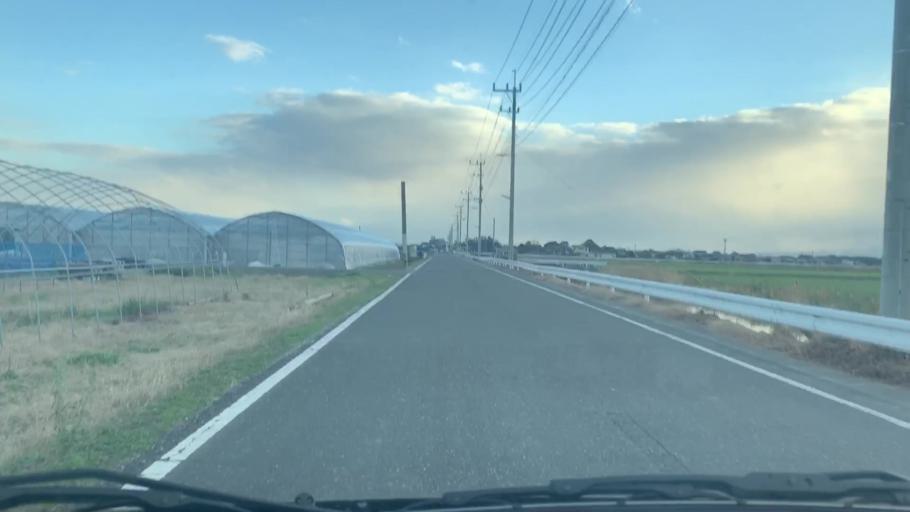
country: JP
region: Saga Prefecture
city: Saga-shi
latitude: 33.2539
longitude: 130.2577
